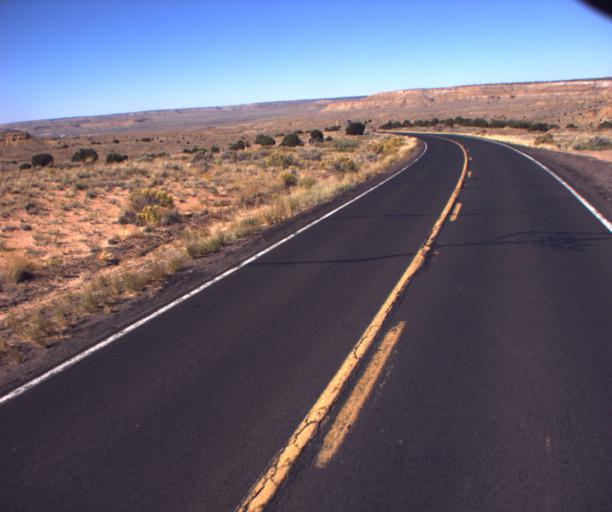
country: US
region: Arizona
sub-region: Navajo County
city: First Mesa
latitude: 35.8623
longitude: -110.5390
